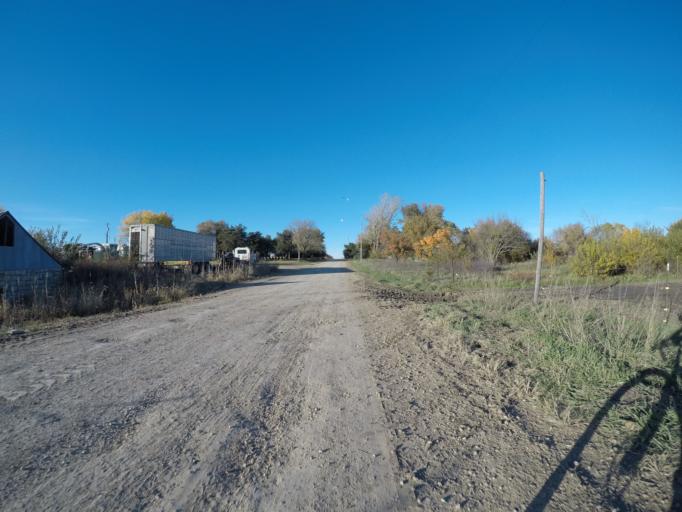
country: US
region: Kansas
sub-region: Riley County
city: Ogden
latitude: 39.2698
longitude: -96.7193
